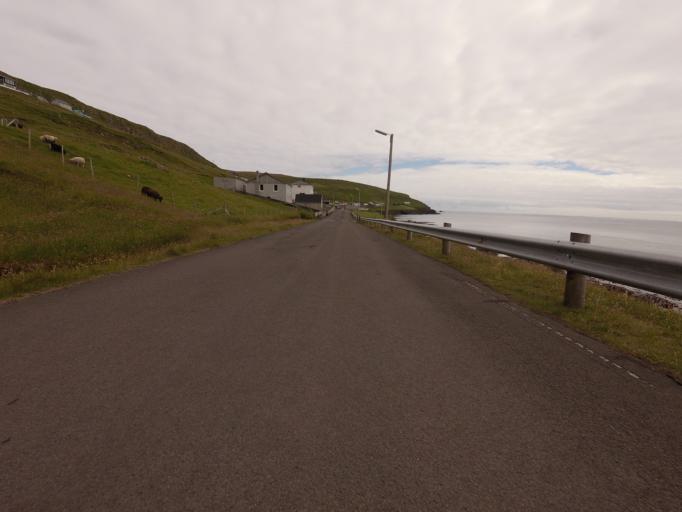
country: FO
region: Suduroy
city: Vagur
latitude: 61.4060
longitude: -6.7240
